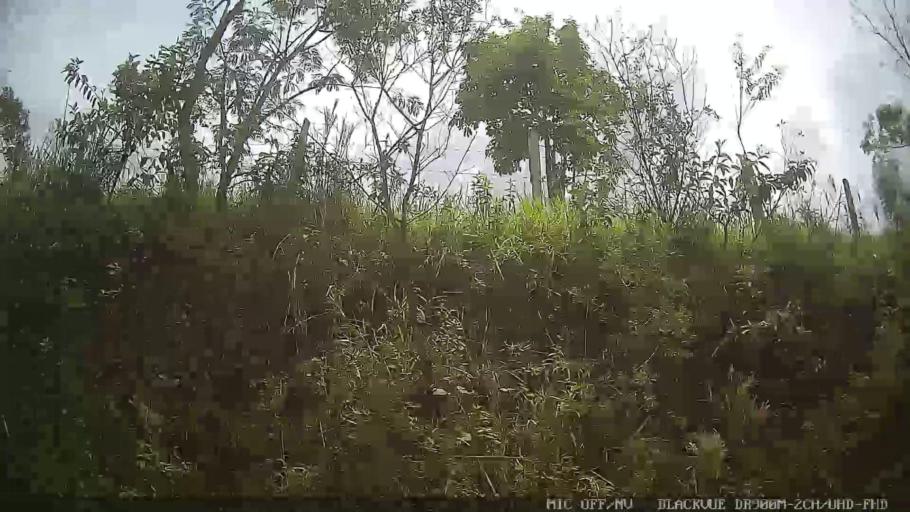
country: BR
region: Sao Paulo
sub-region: Santa Isabel
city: Santa Isabel
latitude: -23.3765
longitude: -46.2390
